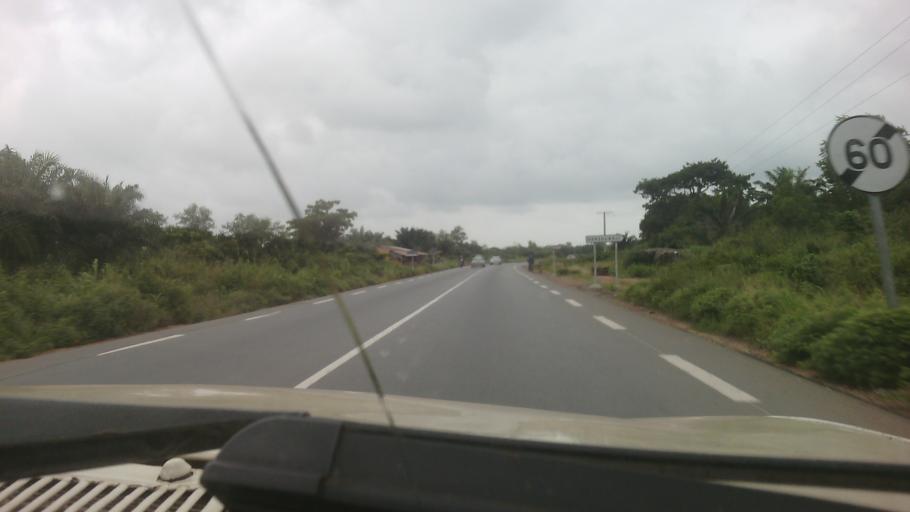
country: BJ
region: Atlantique
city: Ouidah
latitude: 6.3853
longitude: 2.0138
